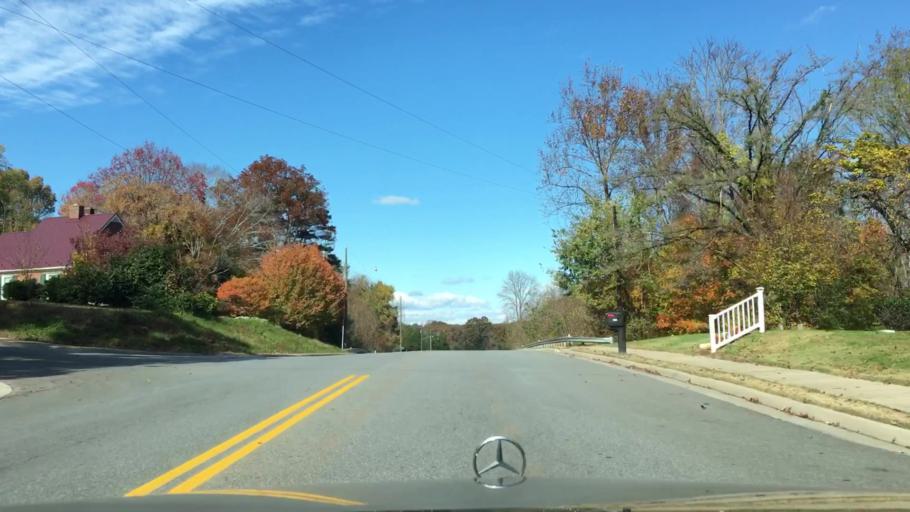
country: US
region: Virginia
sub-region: Campbell County
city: Altavista
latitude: 37.1237
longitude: -79.3046
